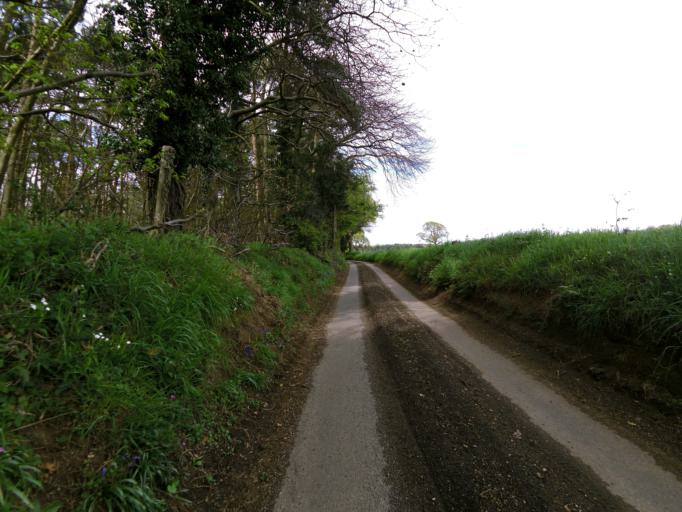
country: GB
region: England
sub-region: Suffolk
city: Ipswich
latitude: 51.9900
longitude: 1.1393
